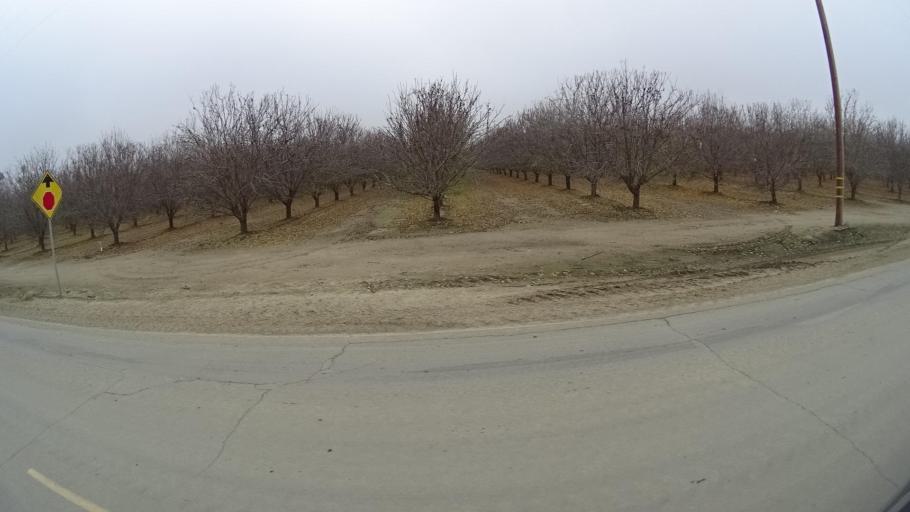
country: US
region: California
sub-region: Kern County
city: Greenfield
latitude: 35.2380
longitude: -119.0590
